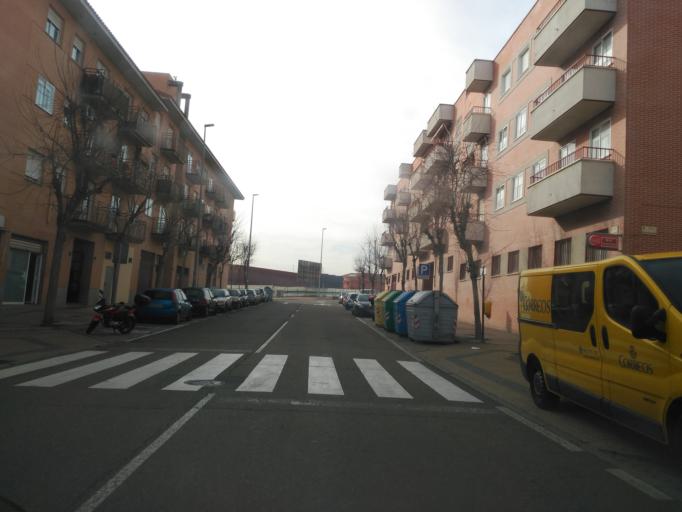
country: ES
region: Castille and Leon
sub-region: Provincia de Salamanca
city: Salamanca
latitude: 40.9604
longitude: -5.6497
